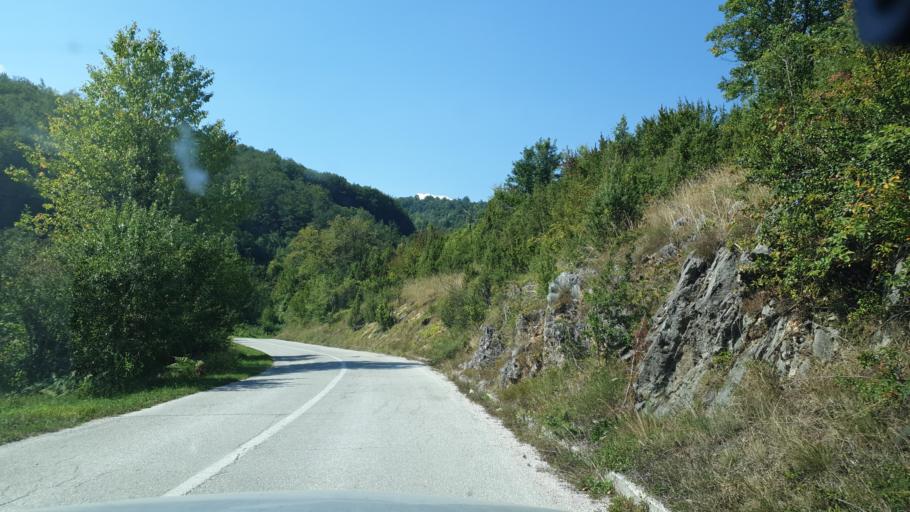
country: RS
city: Zlatibor
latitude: 43.6535
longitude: 19.8255
